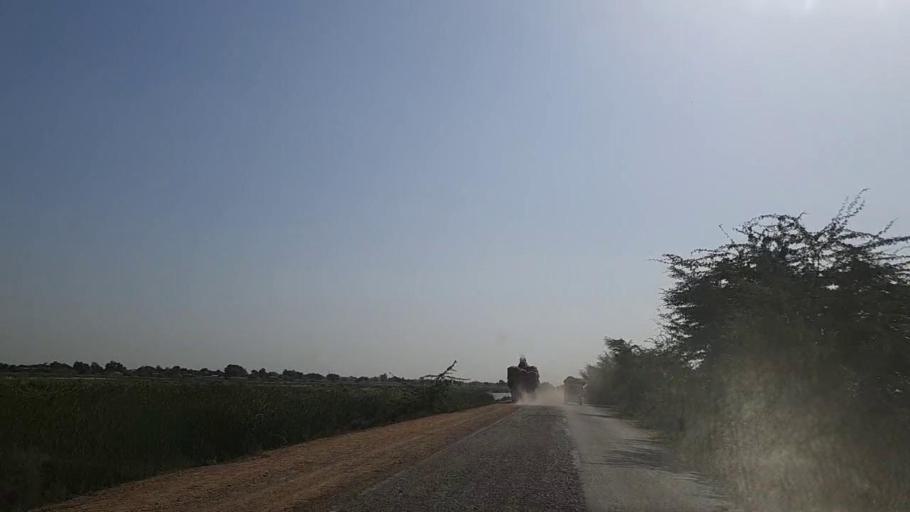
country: PK
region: Sindh
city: Mirpur Batoro
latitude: 24.5815
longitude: 68.2895
